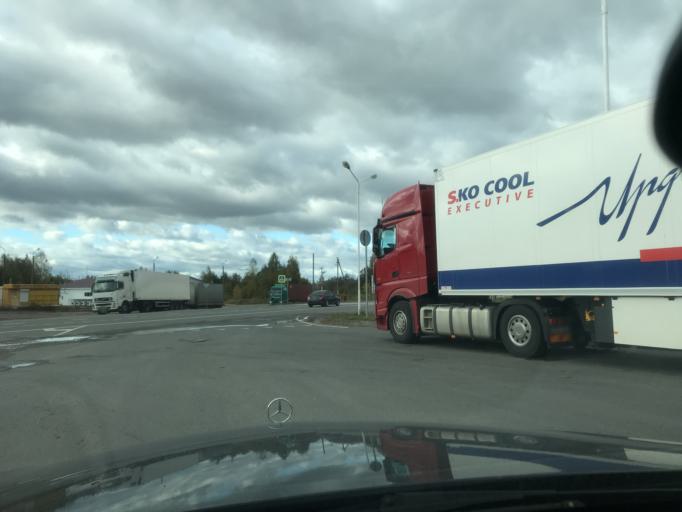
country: RU
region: Pskov
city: Opochka
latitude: 56.7114
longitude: 28.6907
